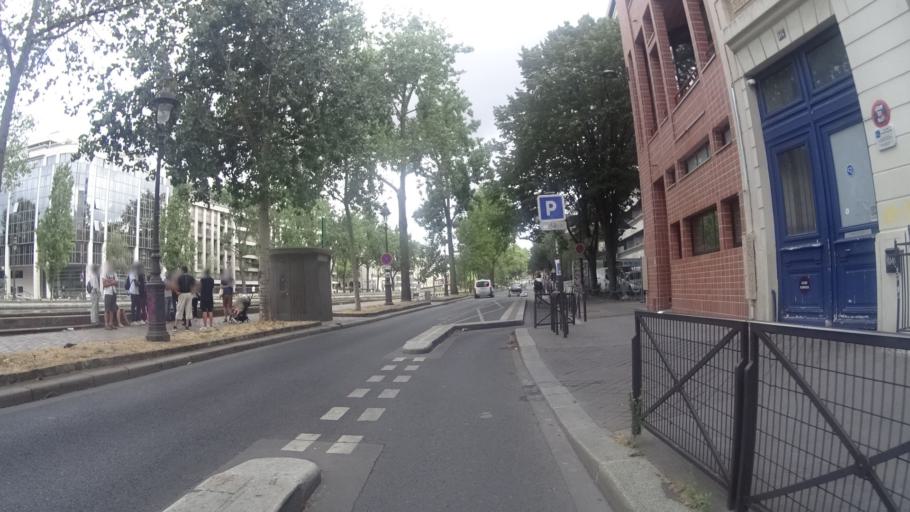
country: FR
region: Ile-de-France
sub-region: Paris
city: Paris
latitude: 48.8746
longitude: 2.3636
